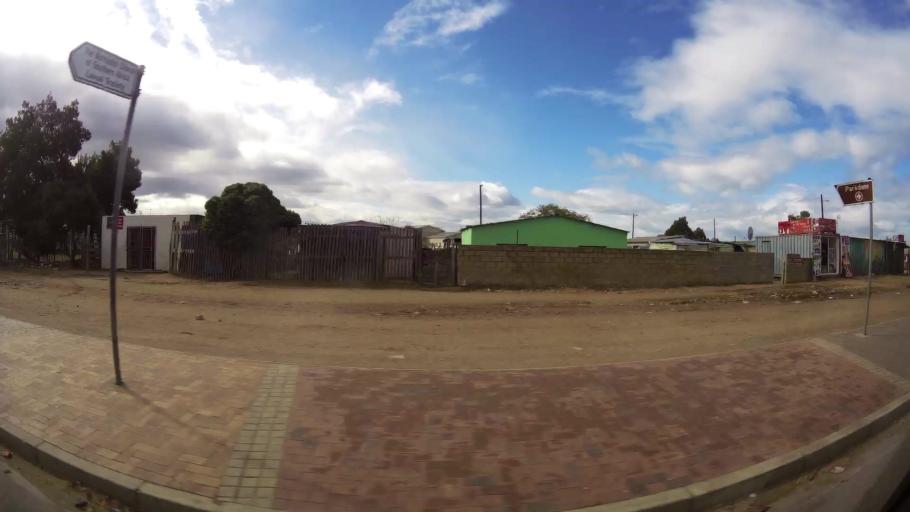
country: ZA
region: Western Cape
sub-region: Eden District Municipality
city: George
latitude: -33.9920
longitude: 22.4746
